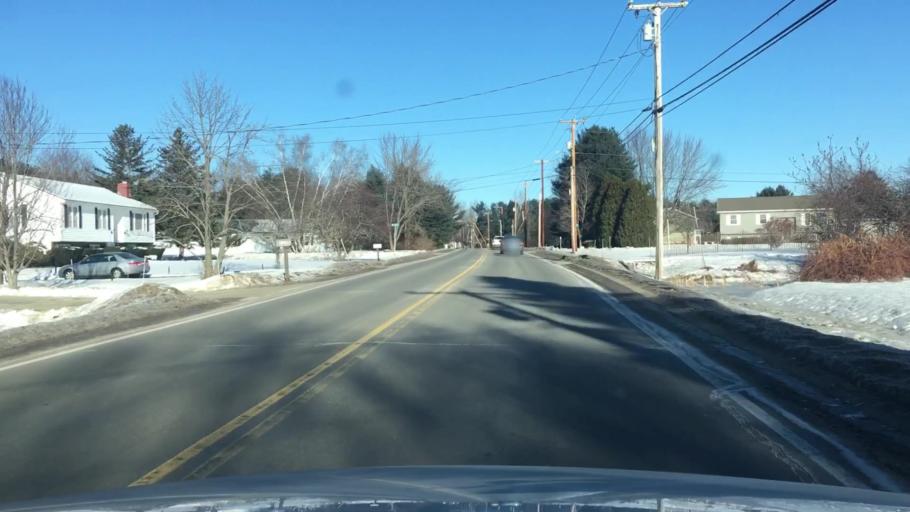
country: US
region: Maine
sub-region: Androscoggin County
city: Auburn
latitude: 44.0932
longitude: -70.2636
